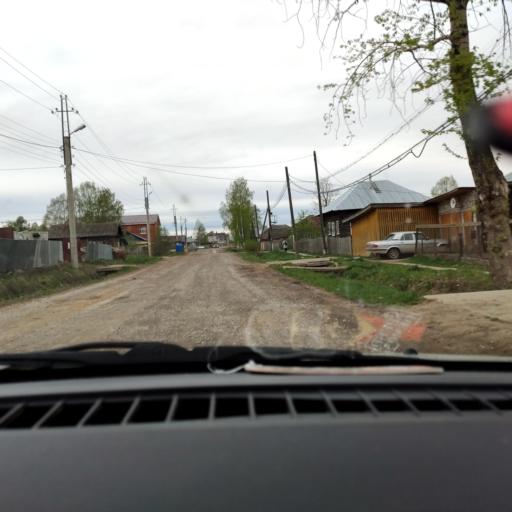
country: RU
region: Perm
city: Kudymkar
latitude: 59.0106
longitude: 54.6380
